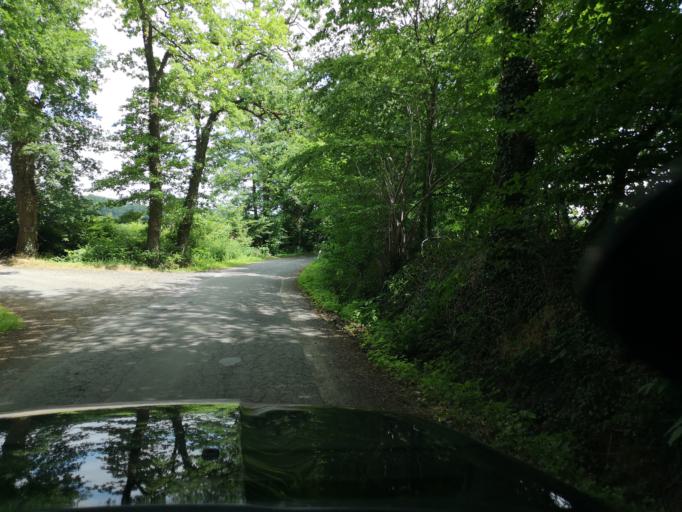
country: DE
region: North Rhine-Westphalia
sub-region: Regierungsbezirk Munster
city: Rhede
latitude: 51.8569
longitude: 6.6852
